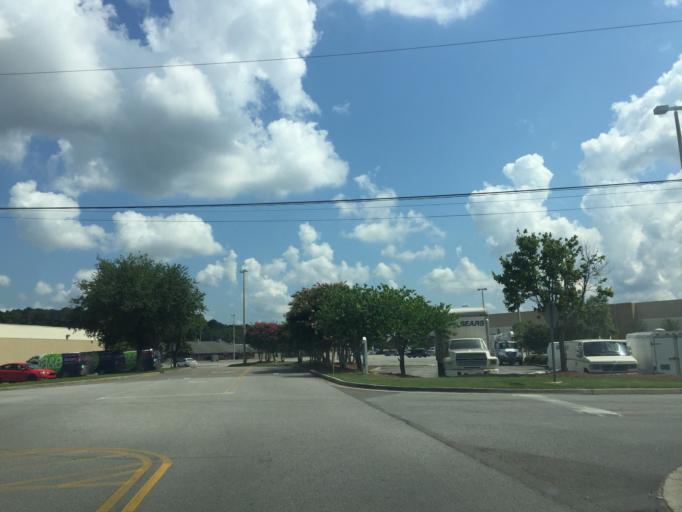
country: US
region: Georgia
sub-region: Chatham County
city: Montgomery
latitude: 32.0009
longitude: -81.1198
